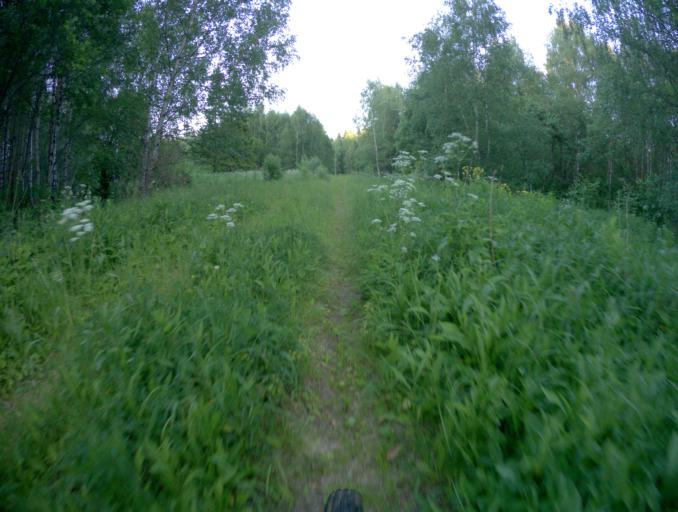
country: RU
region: Vladimir
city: Stavrovo
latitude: 56.3184
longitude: 39.9575
